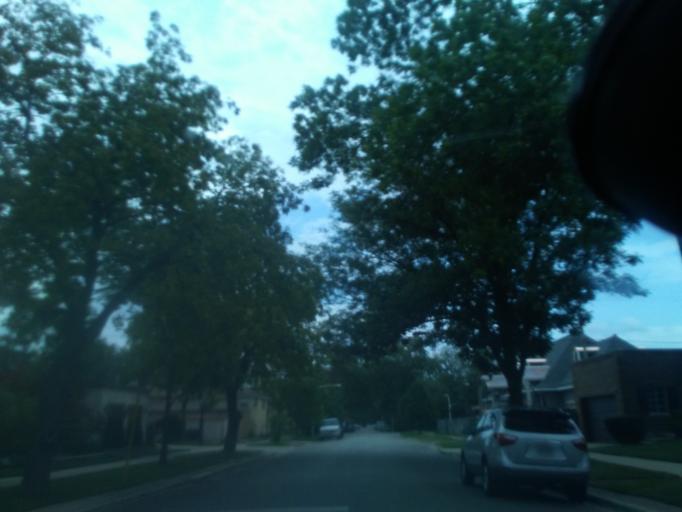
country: US
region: Illinois
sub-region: Cook County
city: Lincolnwood
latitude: 41.9920
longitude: -87.7176
